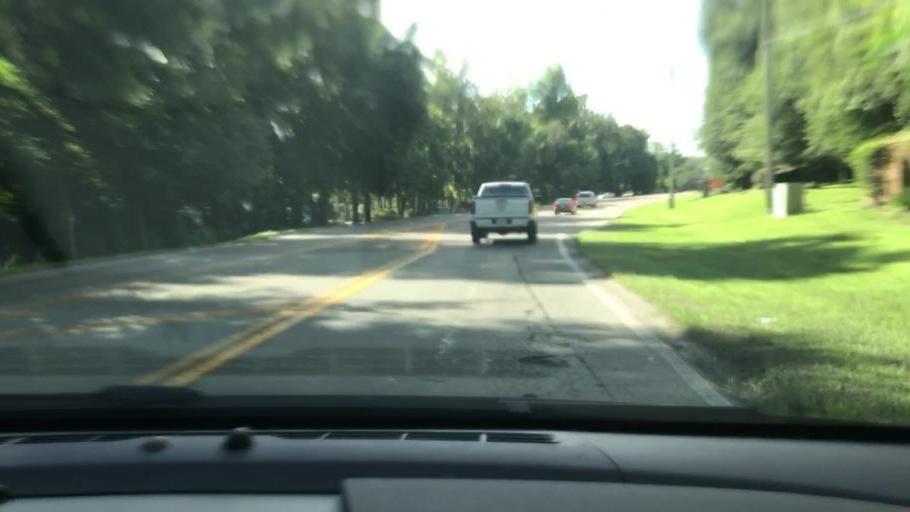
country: US
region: Florida
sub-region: Alachua County
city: Gainesville
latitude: 29.6432
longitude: -82.3988
